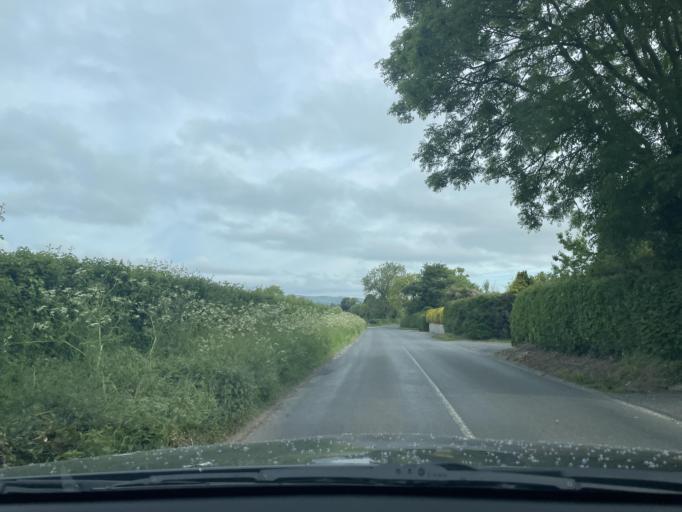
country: IE
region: Leinster
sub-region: County Carlow
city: Bagenalstown
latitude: 52.6465
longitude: -6.9720
